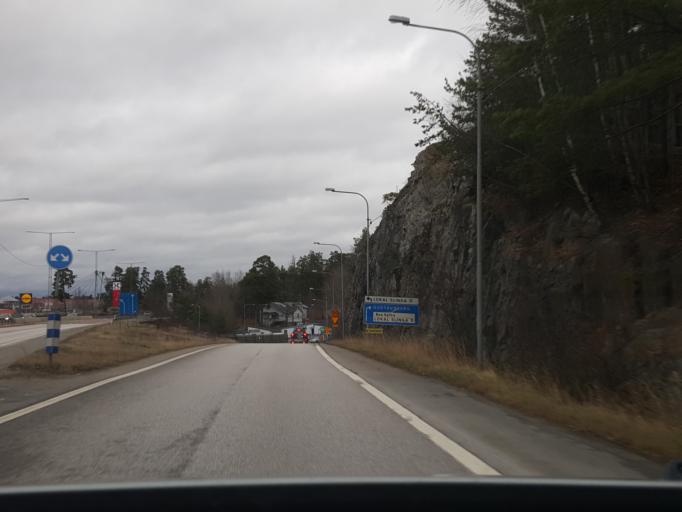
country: SE
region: Stockholm
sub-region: Nacka Kommun
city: Boo
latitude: 59.3211
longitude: 18.2576
